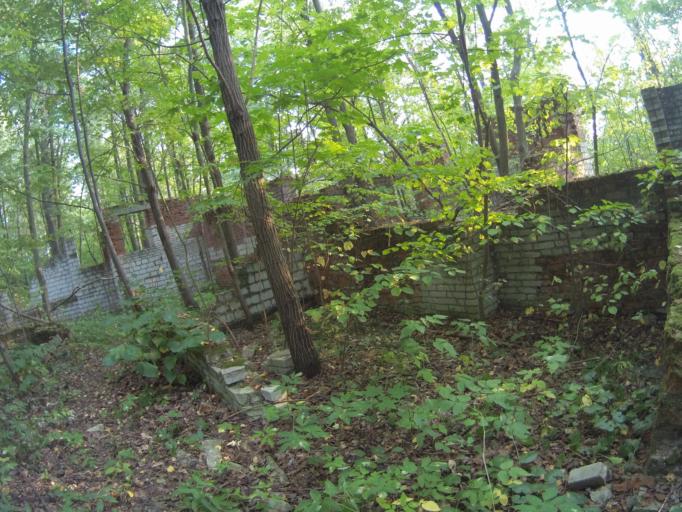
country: RU
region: Vladimir
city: Orgtrud
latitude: 56.1958
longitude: 40.5849
